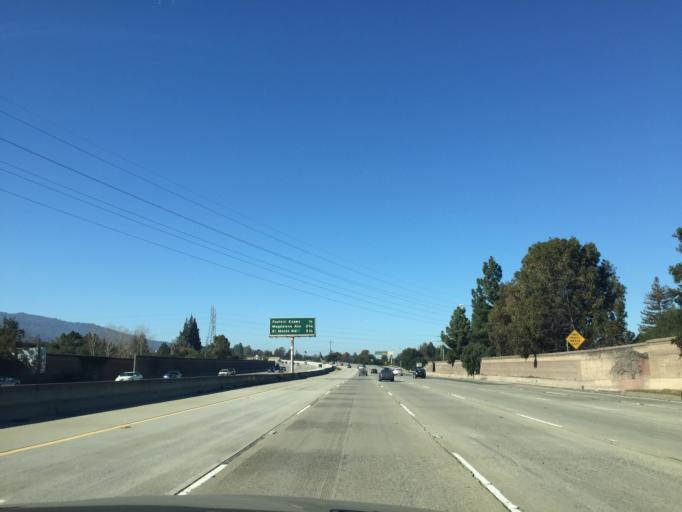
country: US
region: California
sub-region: Santa Clara County
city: Cupertino
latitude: 37.3329
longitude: -122.0616
